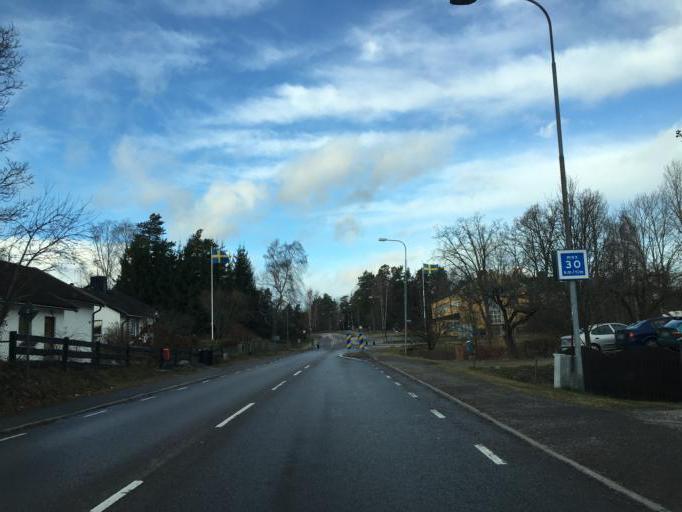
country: SE
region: Kalmar
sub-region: Vasterviks Kommun
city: Vaestervik
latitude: 57.7216
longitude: 16.5250
